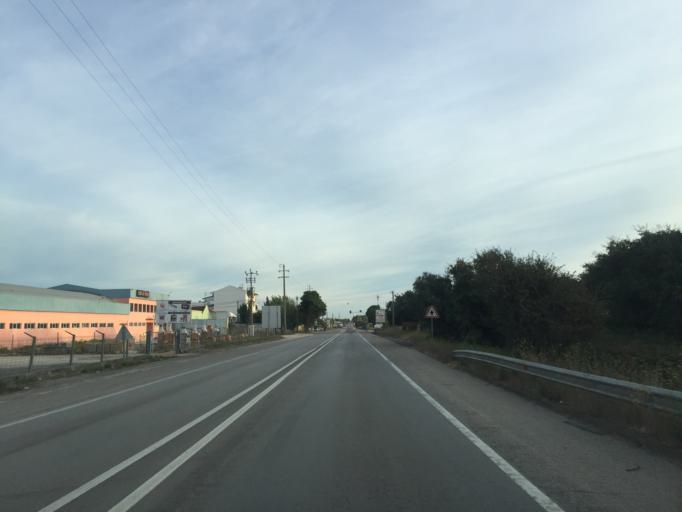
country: PT
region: Leiria
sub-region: Alcobaca
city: Benedita
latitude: 39.4254
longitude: -8.9603
